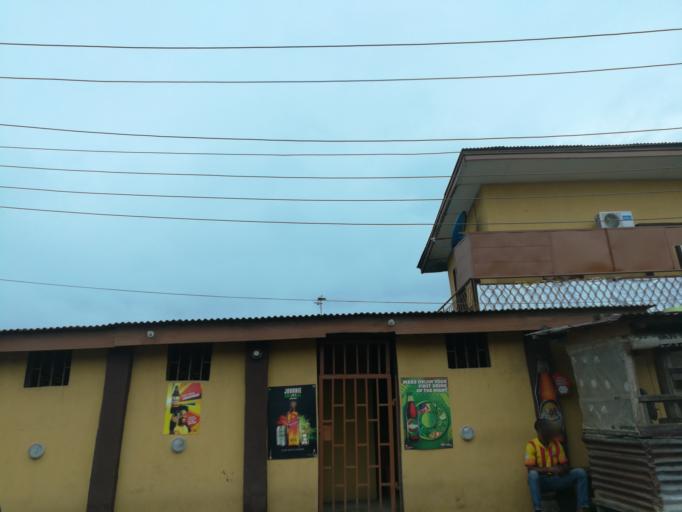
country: NG
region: Lagos
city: Oshodi
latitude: 6.5718
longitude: 3.3445
